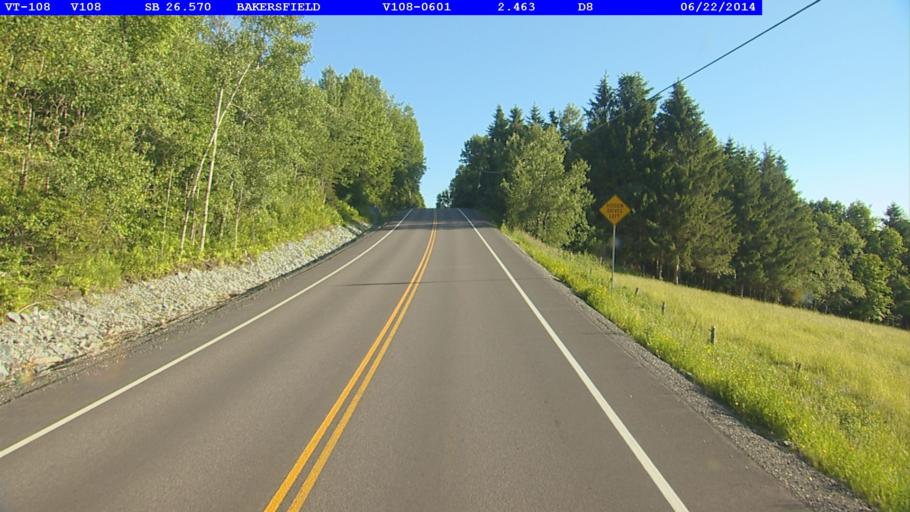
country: US
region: Vermont
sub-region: Franklin County
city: Enosburg Falls
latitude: 44.7671
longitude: -72.8135
